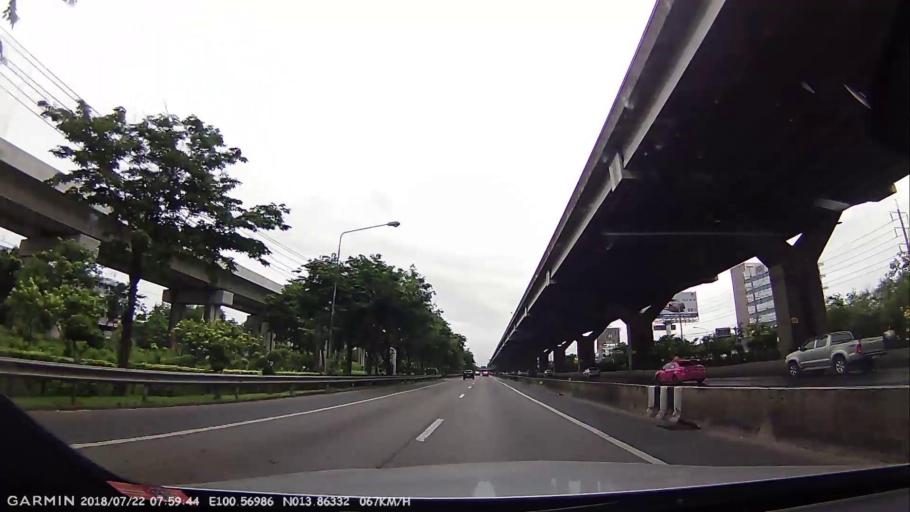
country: TH
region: Bangkok
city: Lak Si
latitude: 13.8636
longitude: 100.5699
